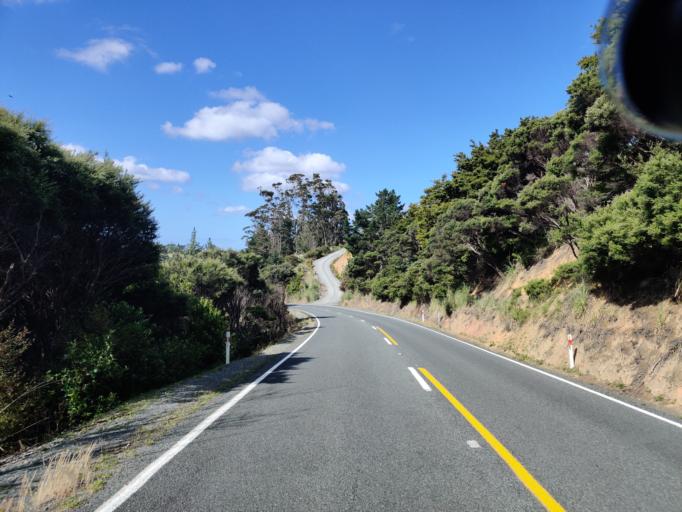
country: NZ
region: Northland
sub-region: Whangarei
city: Ngunguru
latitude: -35.6142
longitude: 174.5217
